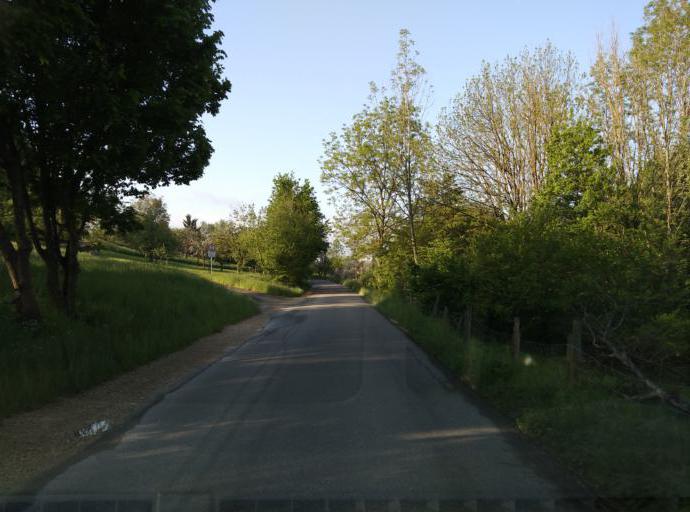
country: DE
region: Baden-Wuerttemberg
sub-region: Tuebingen Region
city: Wannweil
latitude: 48.5062
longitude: 9.1444
